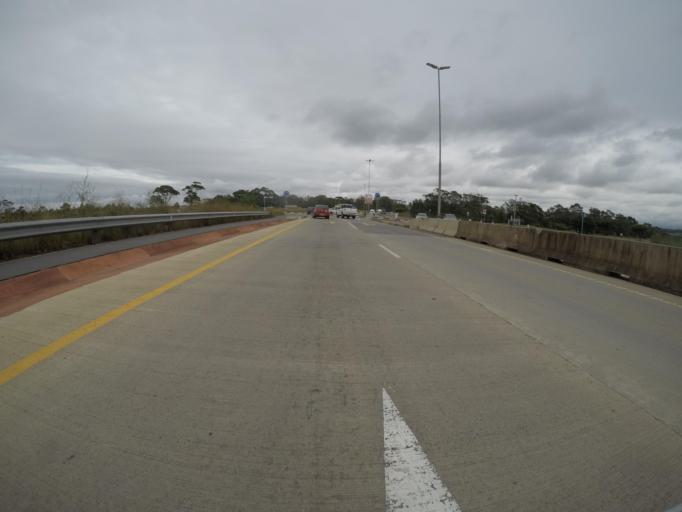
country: ZA
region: Eastern Cape
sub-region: Buffalo City Metropolitan Municipality
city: East London
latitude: -32.9430
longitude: 27.9662
